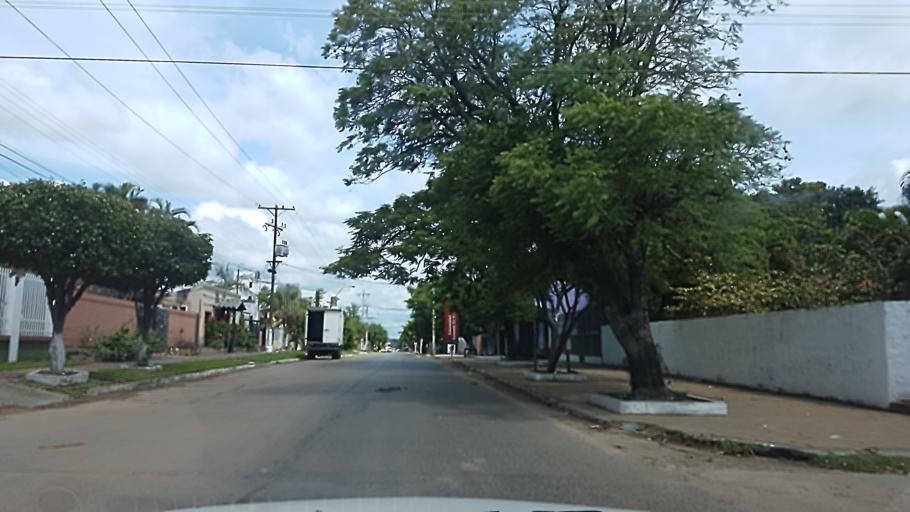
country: PY
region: Central
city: Limpio
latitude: -25.1659
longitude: -57.4756
